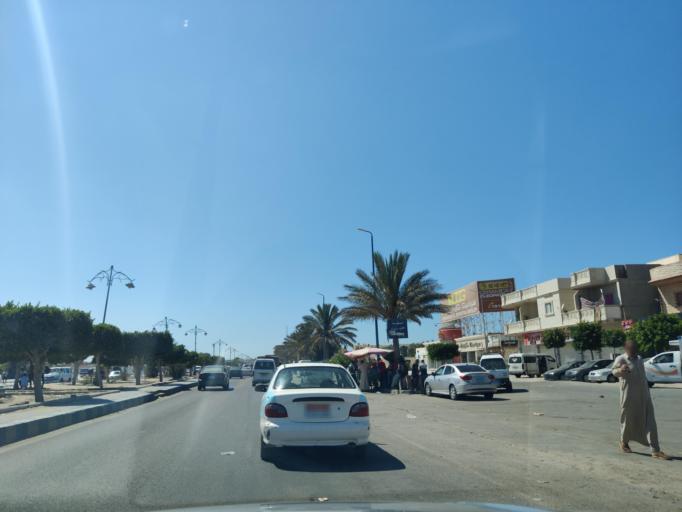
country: EG
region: Muhafazat Matruh
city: Mersa Matruh
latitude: 31.3388
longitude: 27.2510
